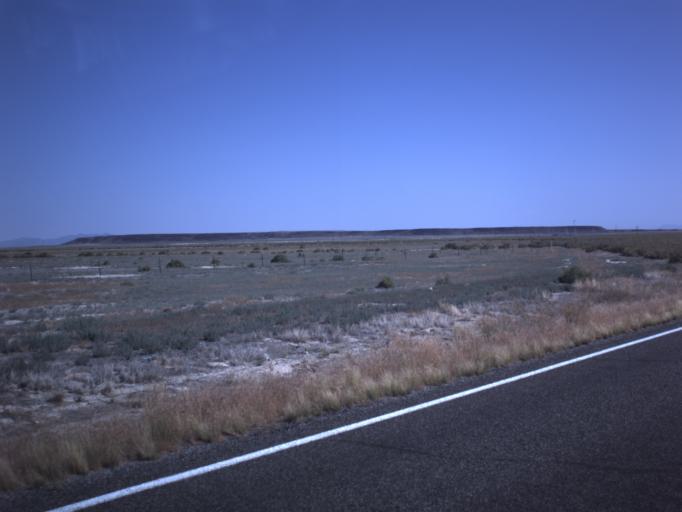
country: US
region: Utah
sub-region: Millard County
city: Delta
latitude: 39.1287
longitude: -112.7328
